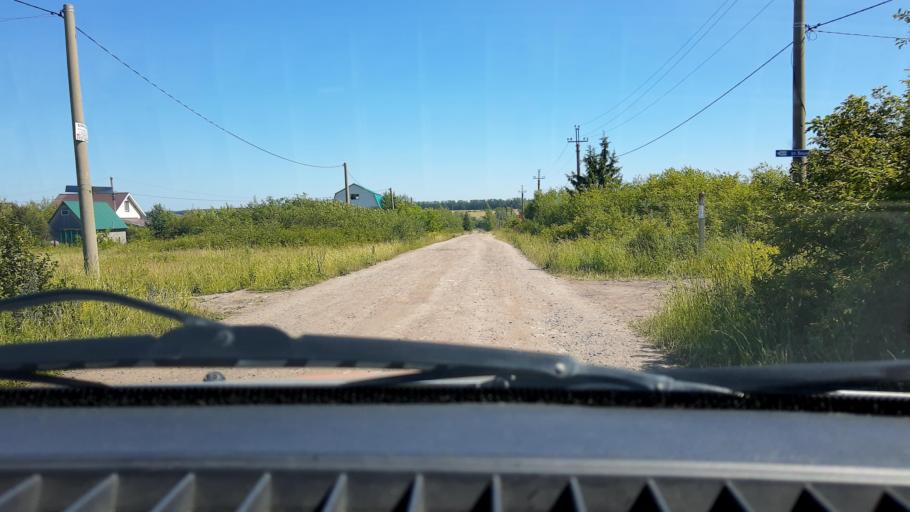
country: RU
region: Bashkortostan
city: Avdon
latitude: 54.5452
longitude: 55.7208
